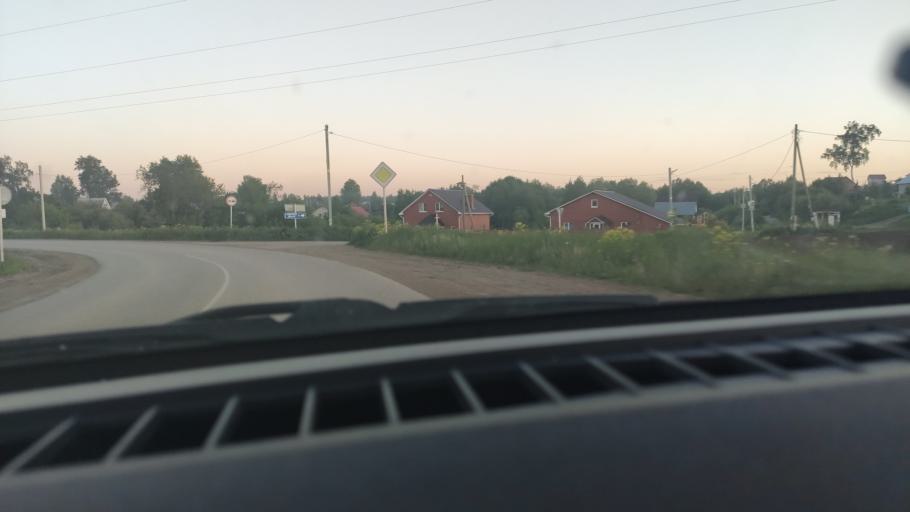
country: RU
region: Perm
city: Kultayevo
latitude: 57.8951
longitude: 55.9148
